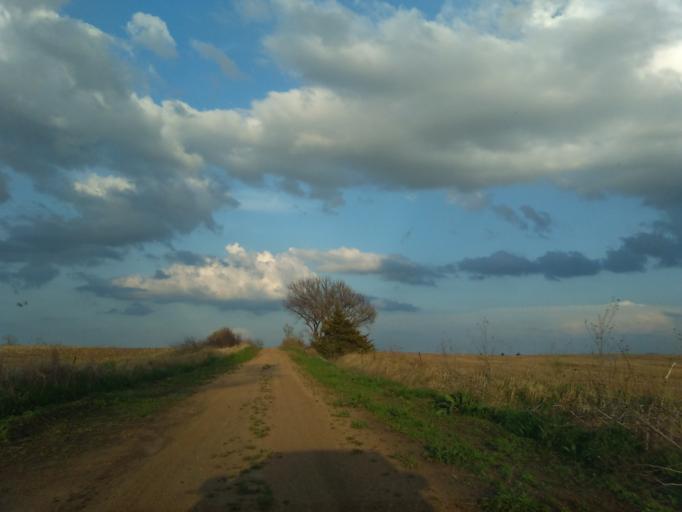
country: US
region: Nebraska
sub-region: Webster County
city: Red Cloud
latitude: 40.2054
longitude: -98.3807
